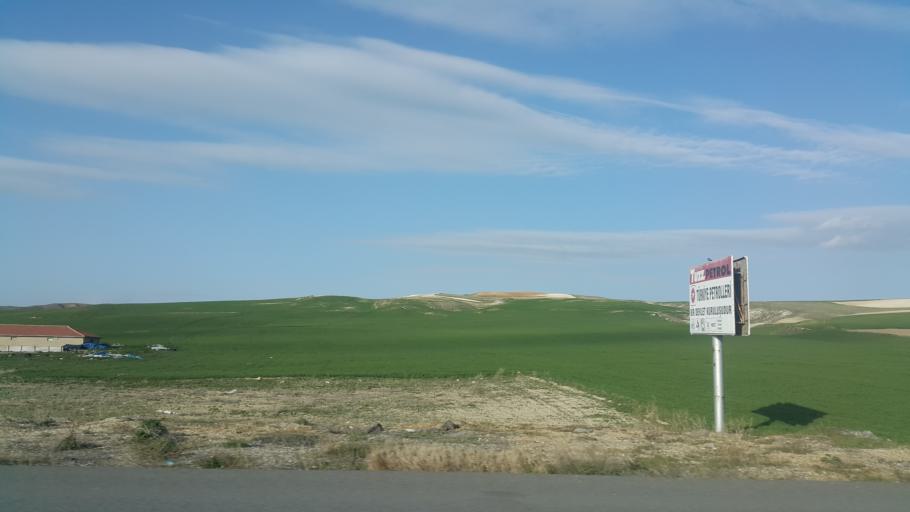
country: TR
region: Ankara
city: Sereflikochisar
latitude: 39.0673
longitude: 33.4212
